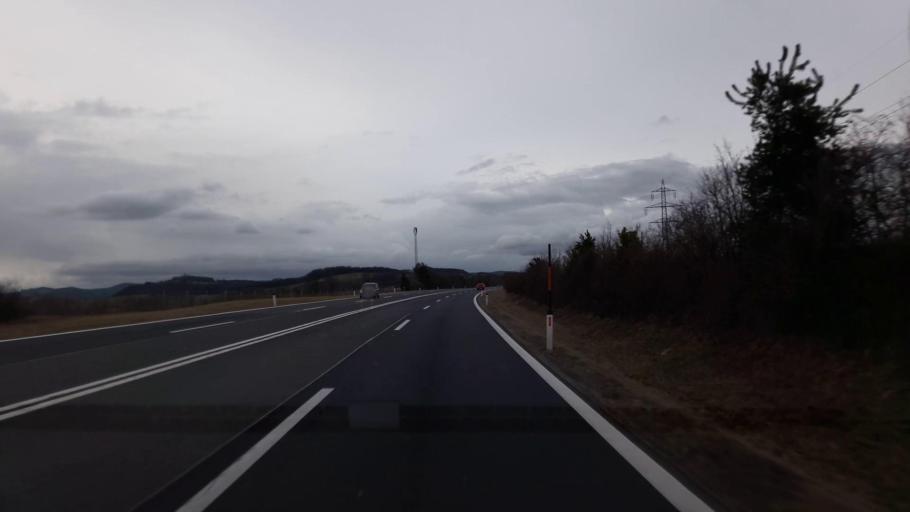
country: AT
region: Burgenland
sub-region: Politischer Bezirk Oberpullendorf
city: Kobersdorf
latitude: 47.6118
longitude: 16.3922
